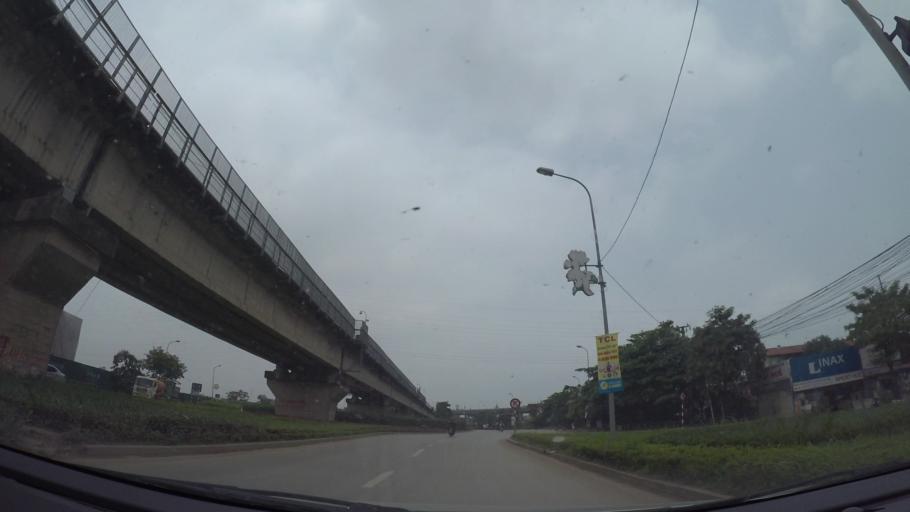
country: VN
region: Ha Noi
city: Tay Ho
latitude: 21.0851
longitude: 105.7859
